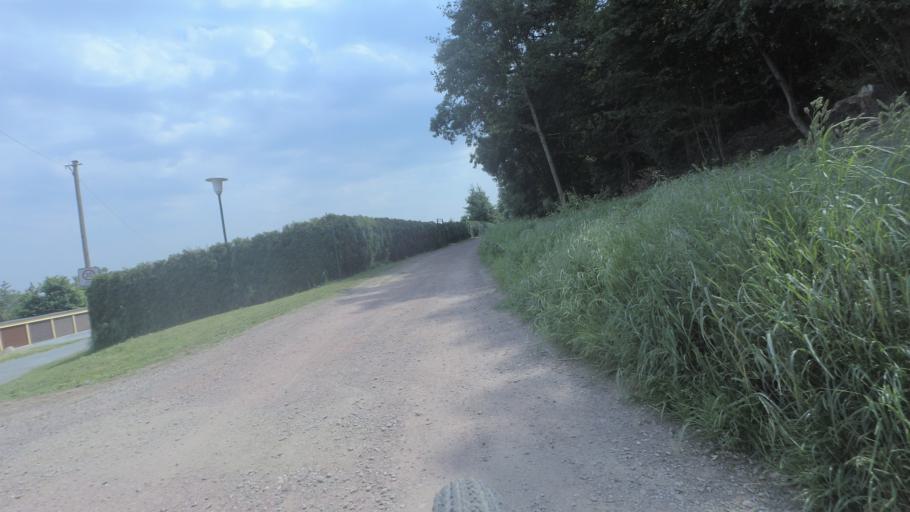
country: DE
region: Saxony-Anhalt
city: Thale
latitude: 51.7463
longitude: 11.0461
